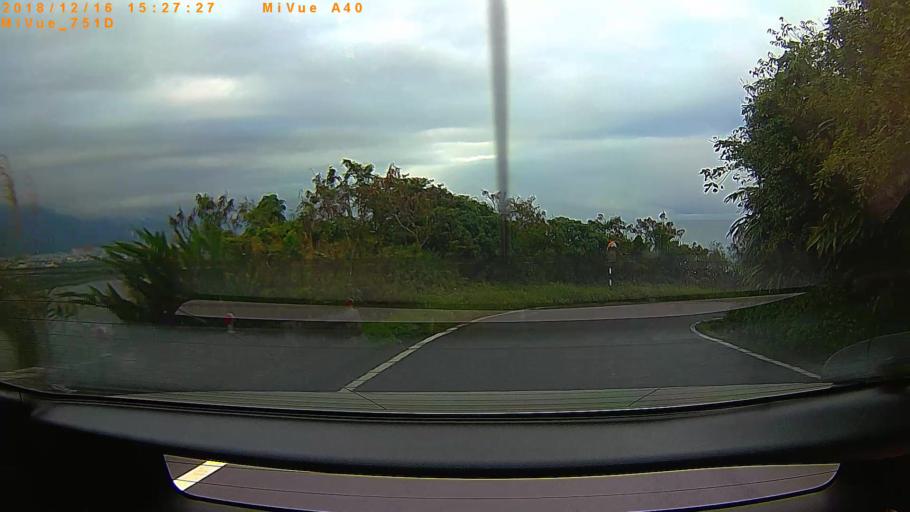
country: TW
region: Taiwan
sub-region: Hualien
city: Hualian
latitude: 23.9235
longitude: 121.6034
